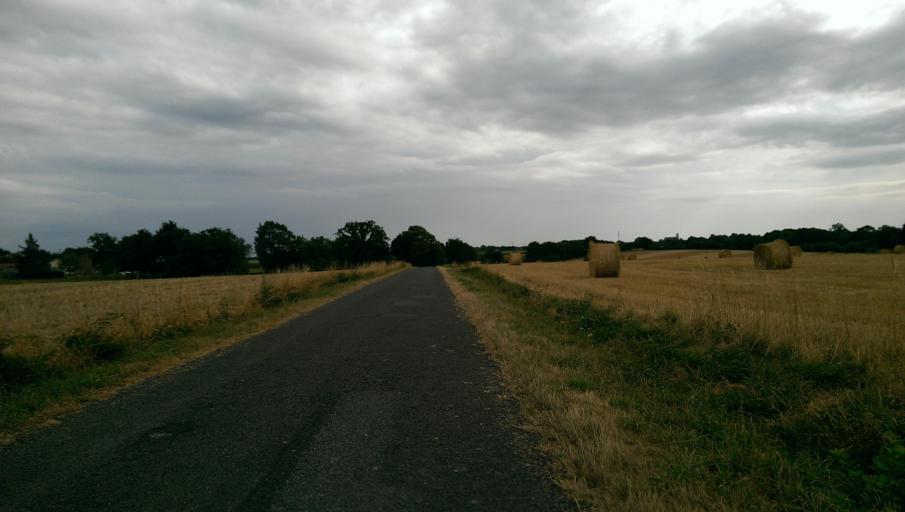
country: FR
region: Pays de la Loire
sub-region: Departement de la Loire-Atlantique
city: La Planche
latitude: 46.9935
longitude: -1.4205
